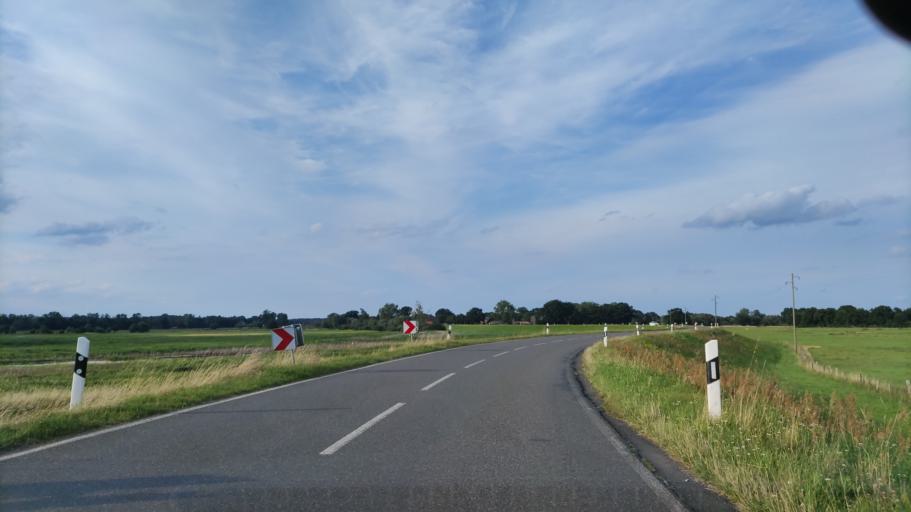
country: DE
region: Lower Saxony
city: Dannenberg
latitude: 53.1298
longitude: 11.1185
